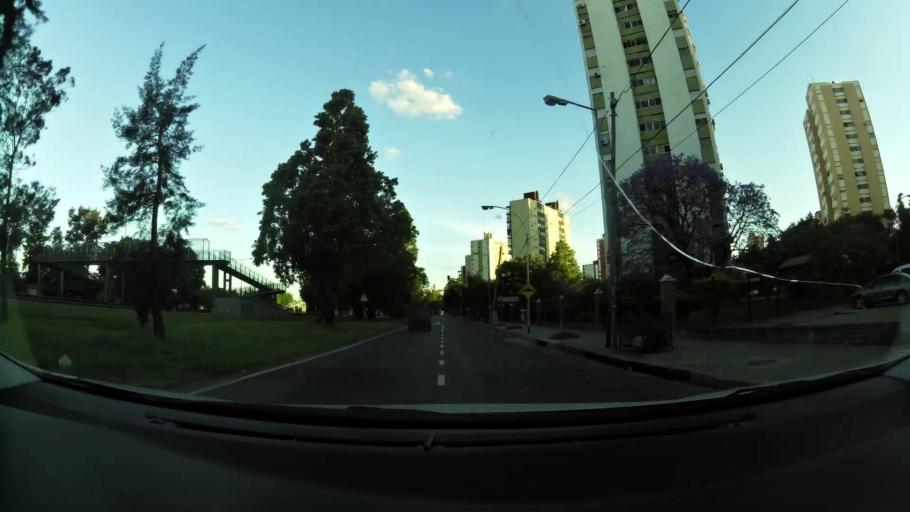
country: AR
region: Buenos Aires F.D.
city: Villa Lugano
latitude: -34.6934
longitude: -58.4775
